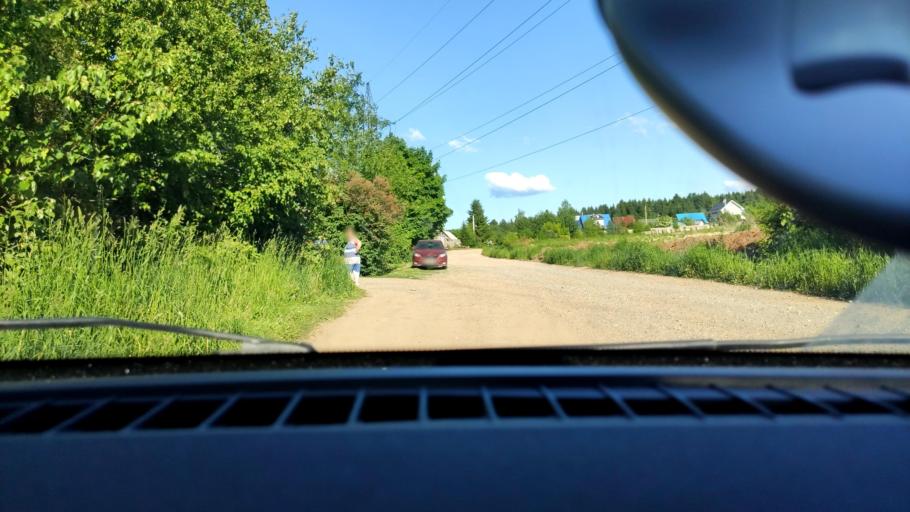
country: RU
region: Perm
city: Ferma
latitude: 57.9158
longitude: 56.3543
